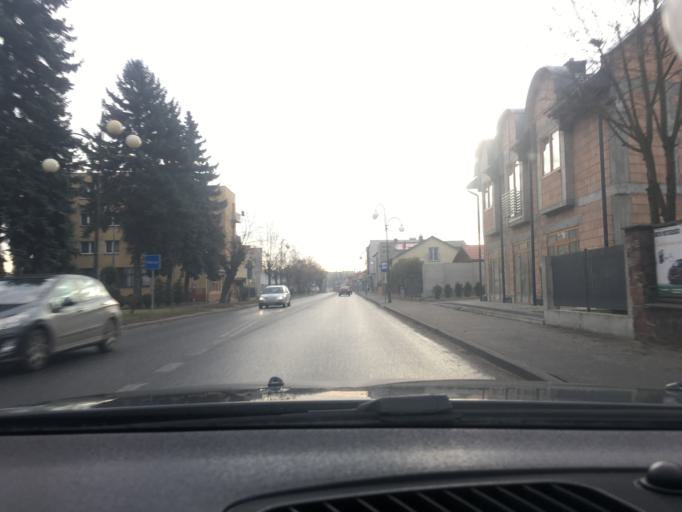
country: PL
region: Swietokrzyskie
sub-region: Powiat jedrzejowski
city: Jedrzejow
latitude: 50.6451
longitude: 20.2950
